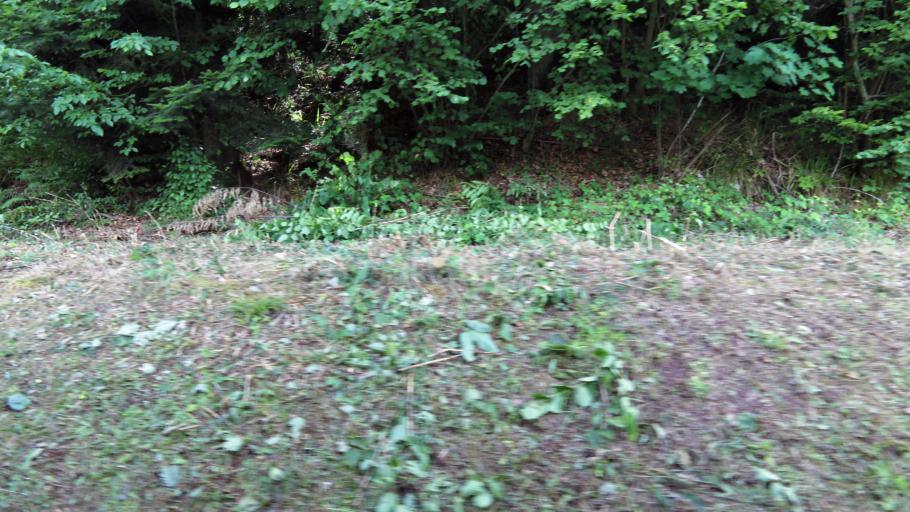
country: FR
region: Lorraine
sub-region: Departement de la Moselle
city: Abreschviller
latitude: 48.6300
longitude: 7.1035
